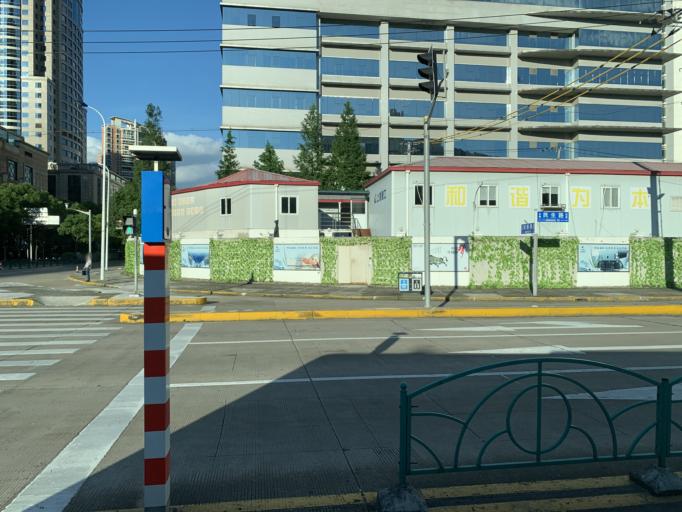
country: CN
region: Shanghai Shi
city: Huamu
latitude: 31.2247
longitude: 121.5461
